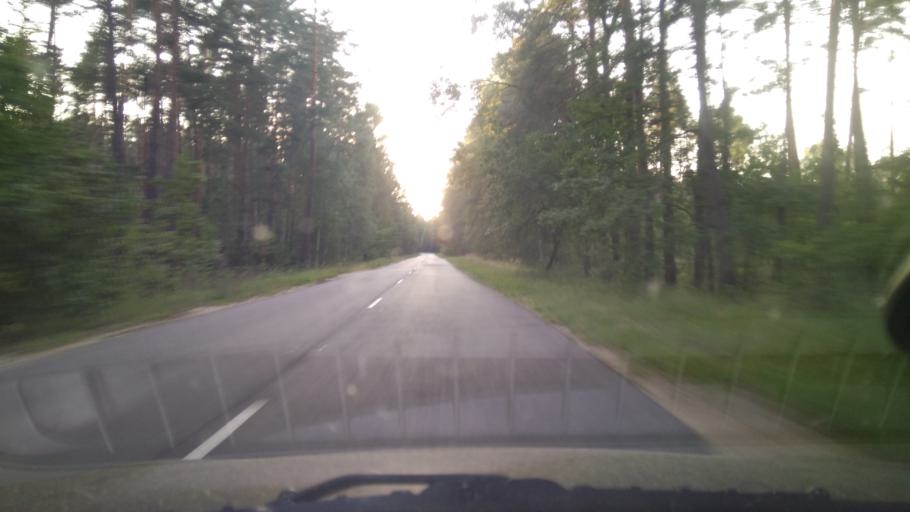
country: BY
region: Brest
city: Nyakhachava
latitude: 52.6001
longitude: 25.0965
